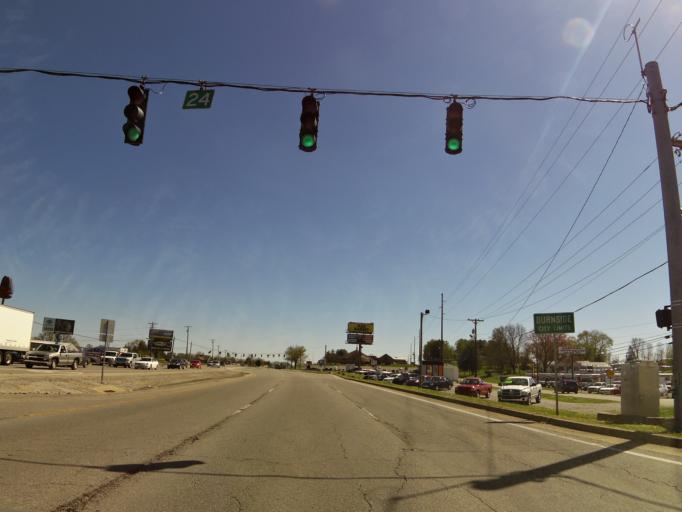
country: US
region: Kentucky
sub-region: Pulaski County
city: Somerset
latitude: 37.0314
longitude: -84.6274
